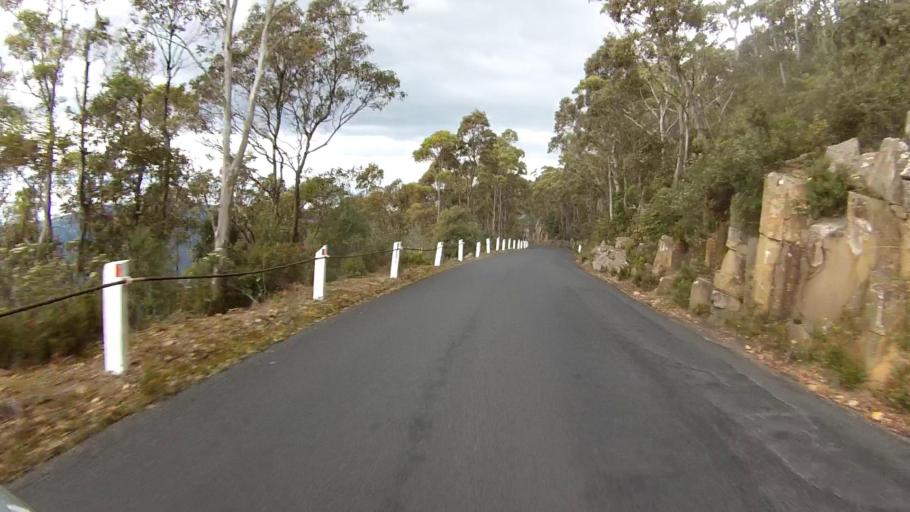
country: AU
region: Tasmania
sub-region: Glenorchy
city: West Moonah
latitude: -42.8920
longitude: 147.2436
